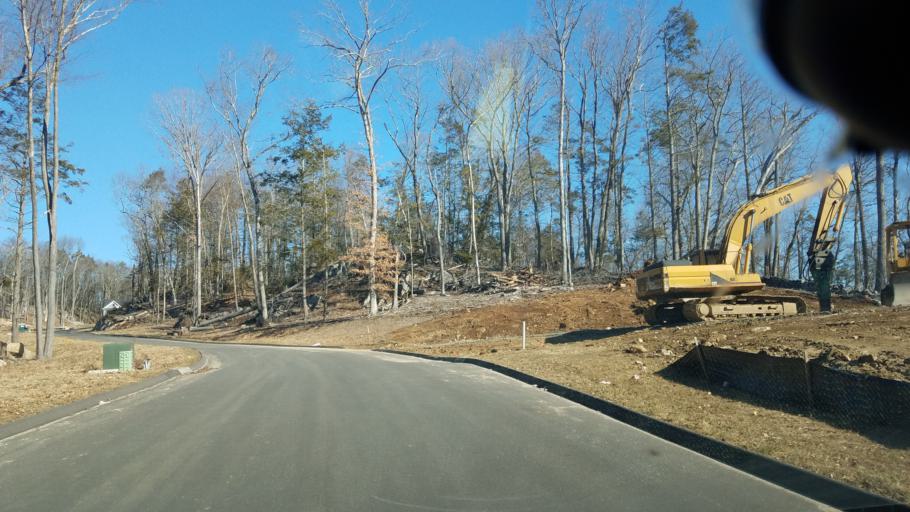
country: US
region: Connecticut
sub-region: Litchfield County
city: New Milford
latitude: 41.4889
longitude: -73.4216
